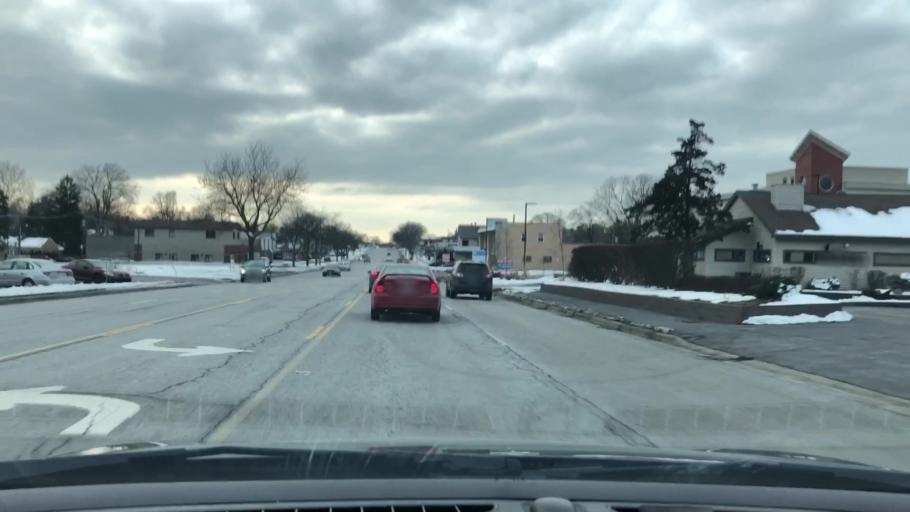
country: US
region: Illinois
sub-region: DuPage County
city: Downers Grove
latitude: 41.8095
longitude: -88.0000
